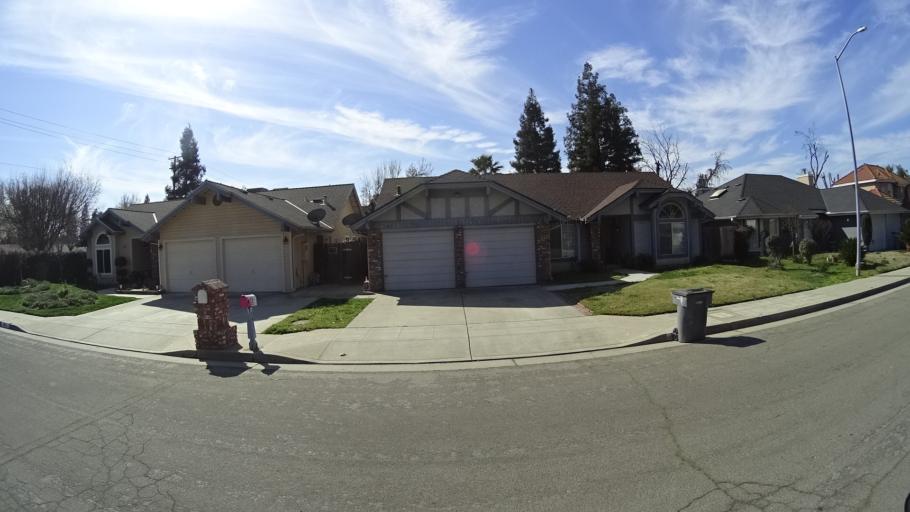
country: US
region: California
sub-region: Fresno County
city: Clovis
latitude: 36.8558
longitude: -119.7483
